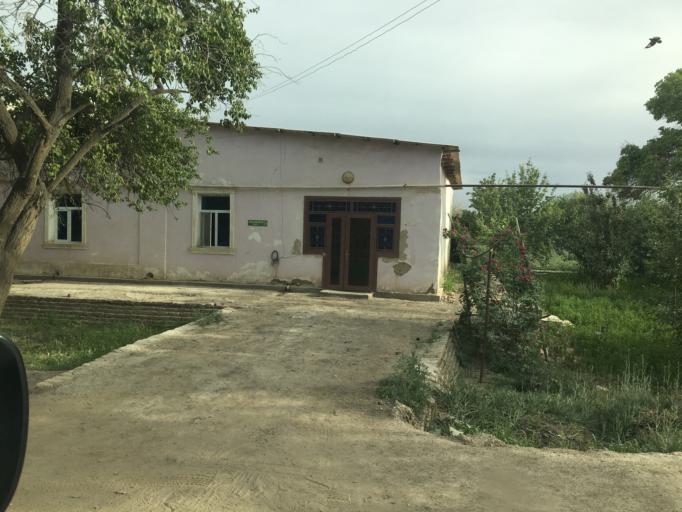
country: TM
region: Dasoguz
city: Dasoguz
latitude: 41.8211
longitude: 59.9149
